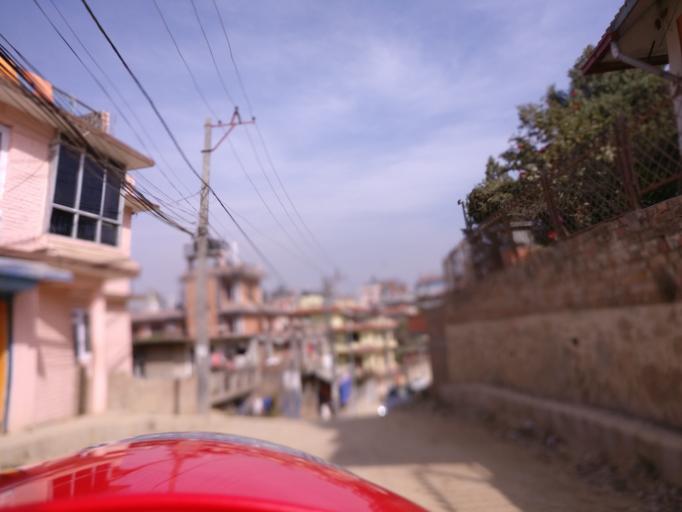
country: NP
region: Central Region
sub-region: Bagmati Zone
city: Patan
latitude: 27.6628
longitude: 85.3121
